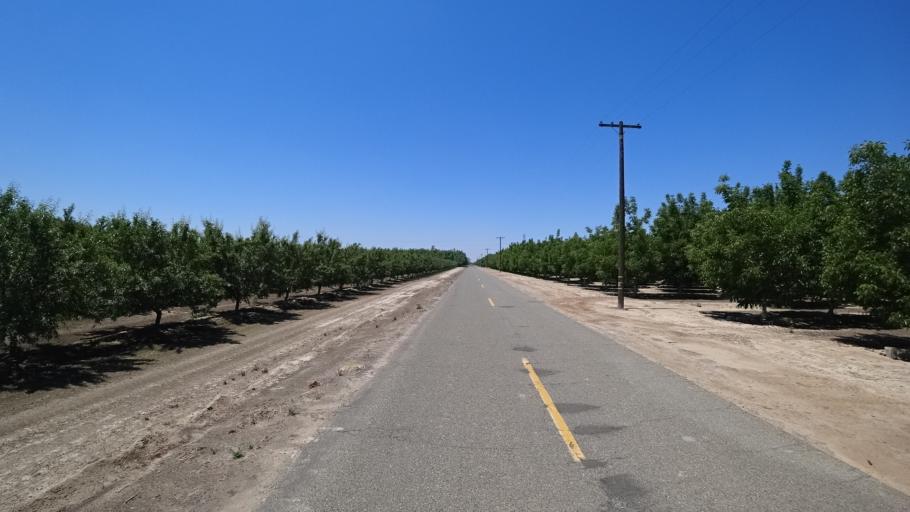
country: US
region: California
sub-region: Fresno County
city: Kingsburg
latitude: 36.4452
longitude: -119.5888
